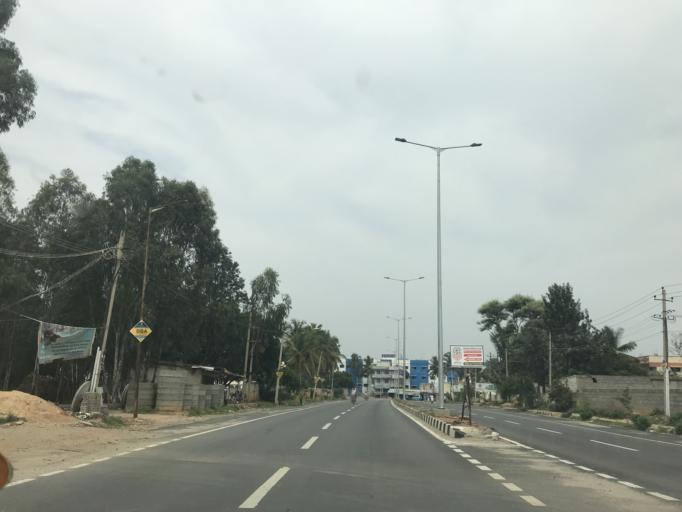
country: IN
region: Karnataka
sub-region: Bangalore Urban
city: Yelahanka
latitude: 13.1061
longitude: 77.6630
